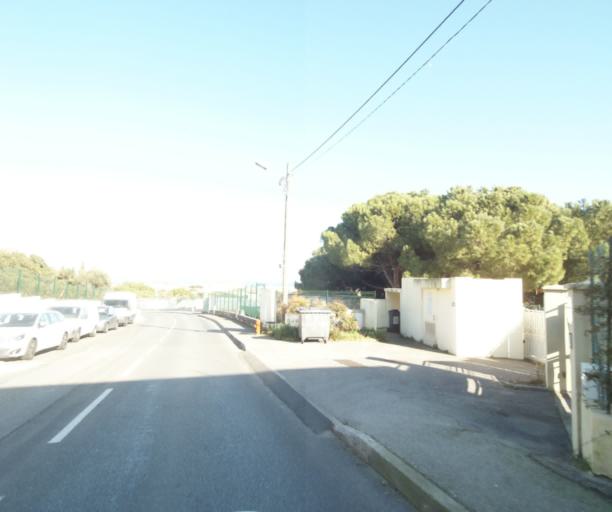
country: FR
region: Provence-Alpes-Cote d'Azur
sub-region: Departement des Alpes-Maritimes
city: Biot
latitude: 43.5997
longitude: 7.1074
